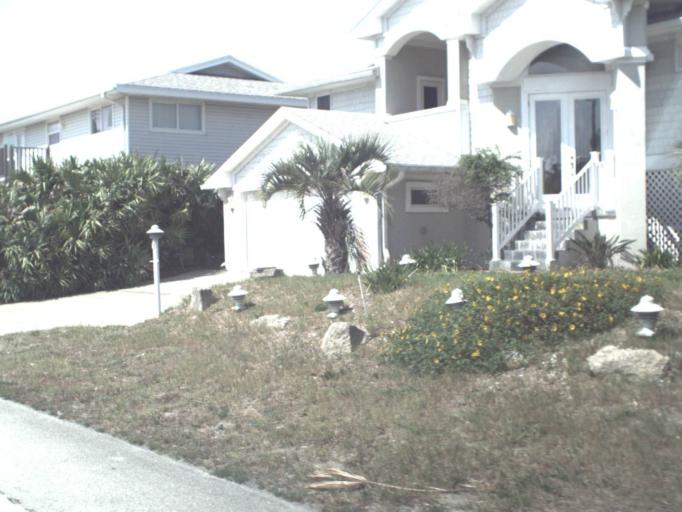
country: US
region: Florida
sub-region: Saint Johns County
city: Villano Beach
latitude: 29.9943
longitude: -81.3162
